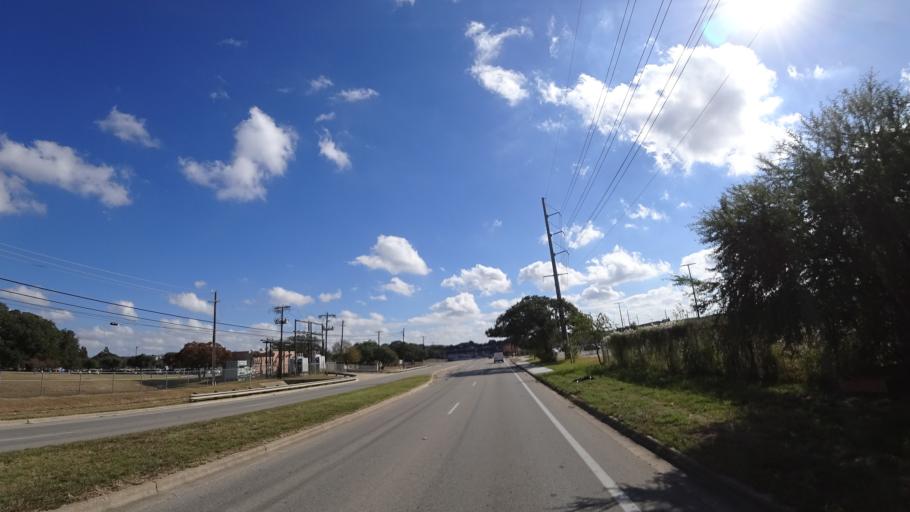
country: US
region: Texas
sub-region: Travis County
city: Wells Branch
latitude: 30.4416
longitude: -97.7030
